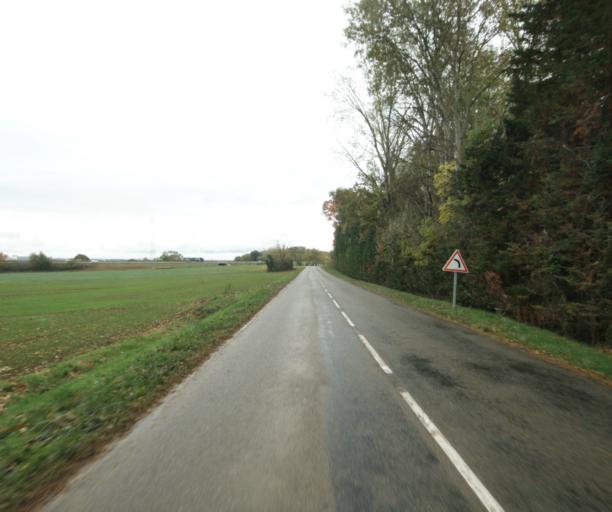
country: FR
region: Rhone-Alpes
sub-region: Departement de l'Ain
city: Pont-de-Vaux
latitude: 46.4628
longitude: 4.8735
